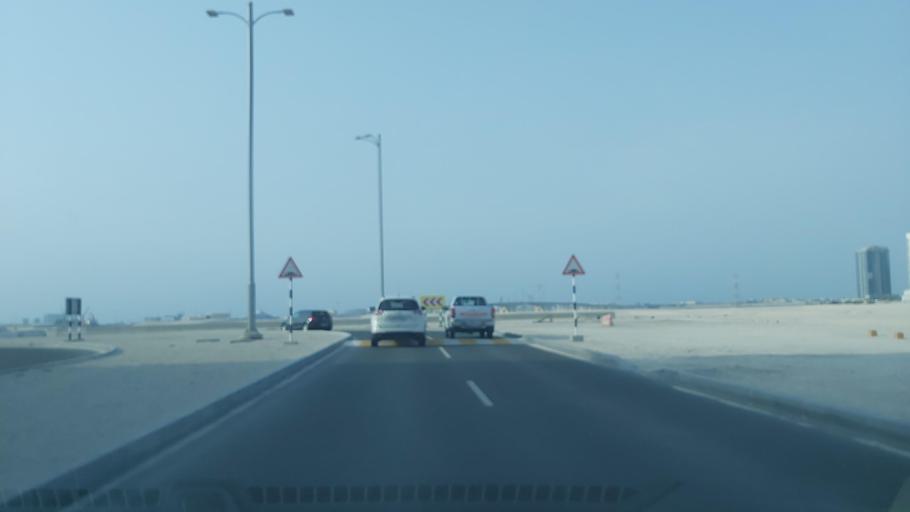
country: AE
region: Abu Dhabi
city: Abu Dhabi
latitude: 24.5021
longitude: 54.3962
